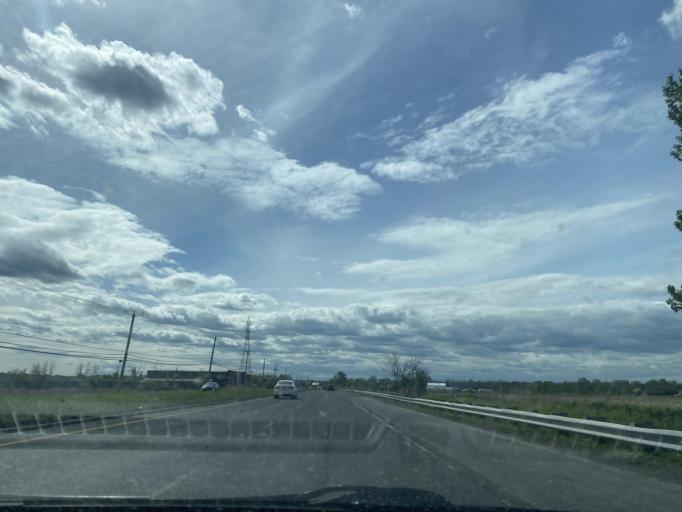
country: CA
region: Quebec
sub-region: Monteregie
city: Carignan
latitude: 45.4611
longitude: -73.3218
